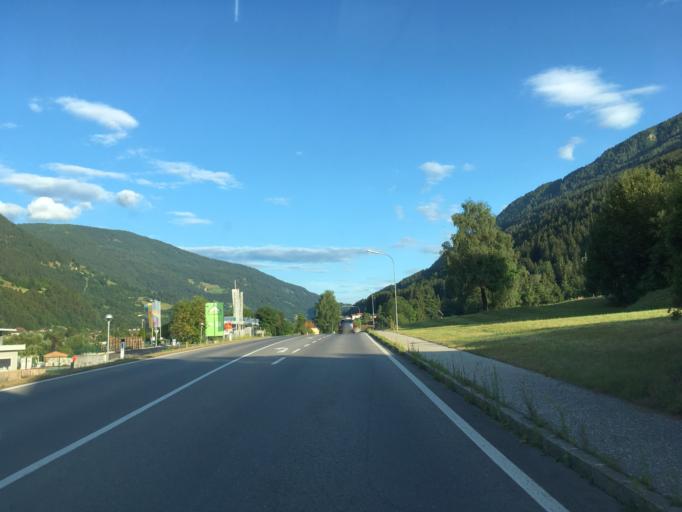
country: AT
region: Carinthia
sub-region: Politischer Bezirk Spittal an der Drau
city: Radenthein
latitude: 46.7953
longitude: 13.7198
